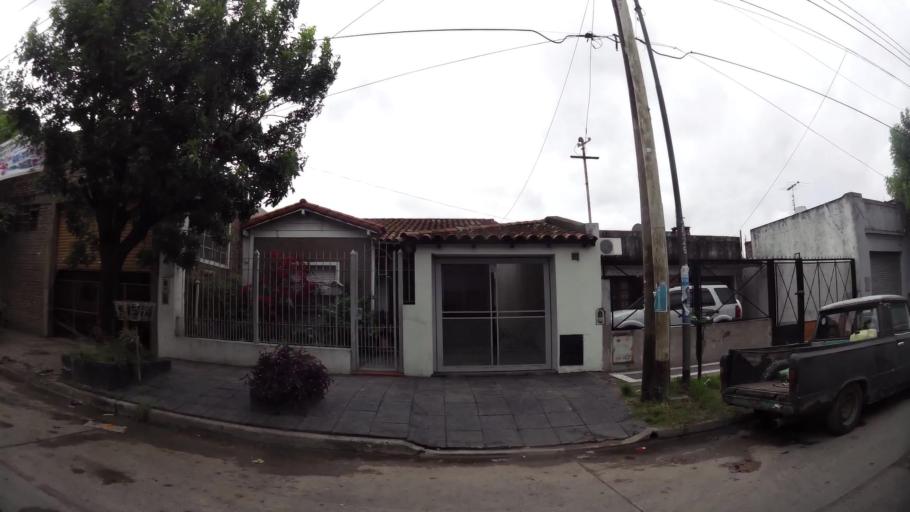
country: AR
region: Buenos Aires
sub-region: Partido de Lanus
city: Lanus
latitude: -34.7293
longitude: -58.3707
